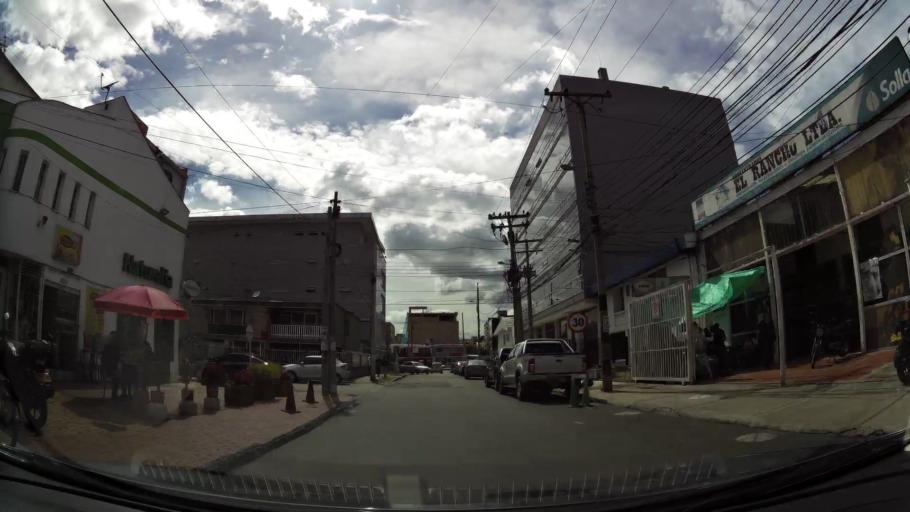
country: CO
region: Bogota D.C.
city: Barrio San Luis
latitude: 4.6868
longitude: -74.0601
